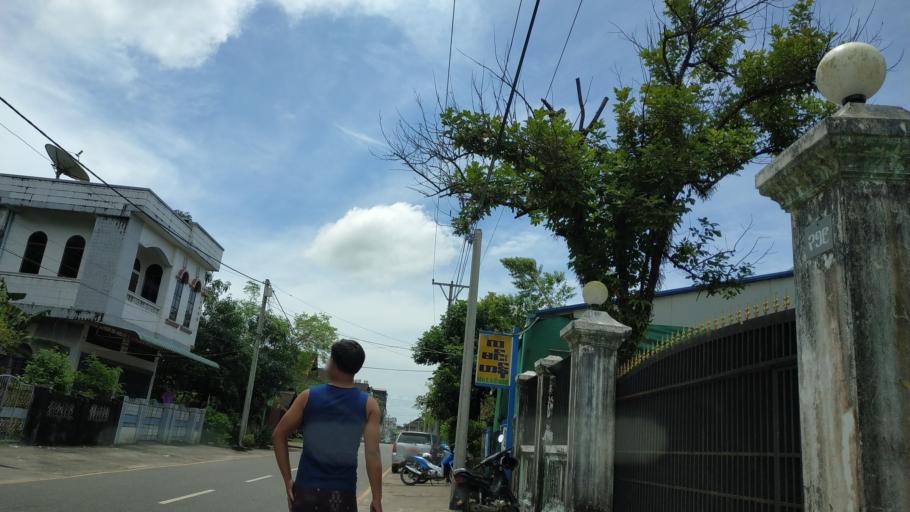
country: MM
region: Tanintharyi
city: Dawei
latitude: 14.0743
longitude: 98.1883
